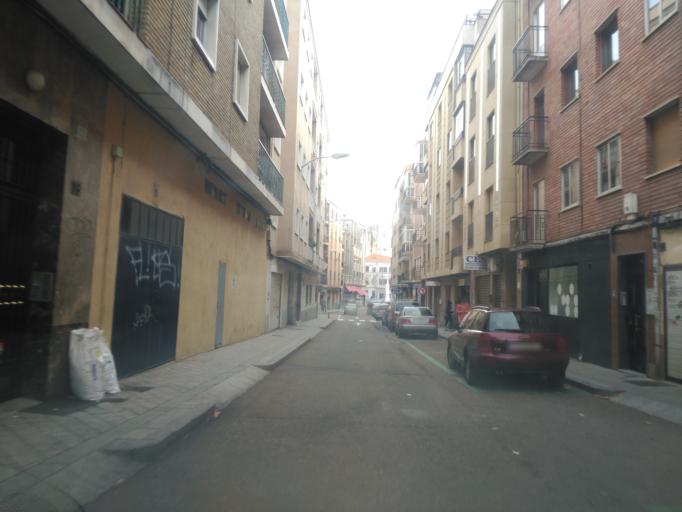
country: ES
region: Castille and Leon
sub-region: Provincia de Salamanca
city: Salamanca
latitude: 40.9707
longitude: -5.6691
